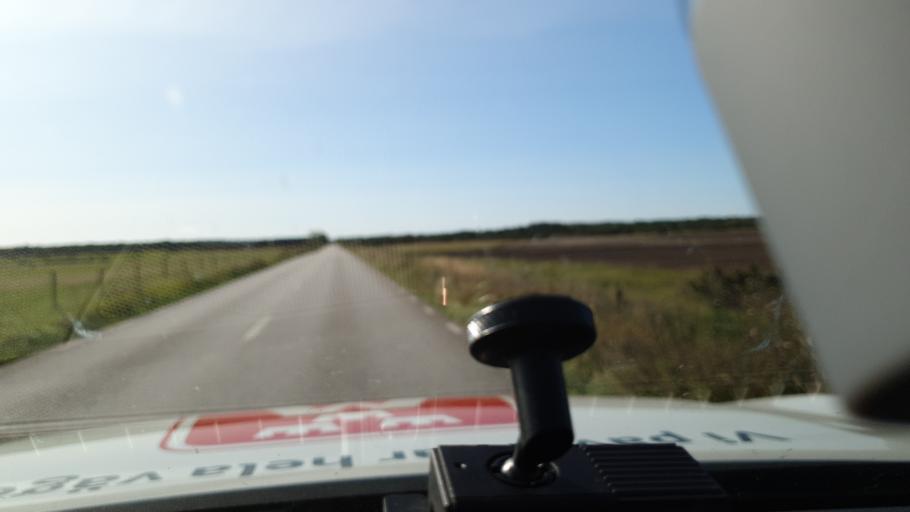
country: SE
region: Gotland
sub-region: Gotland
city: Hemse
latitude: 57.1342
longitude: 18.2815
